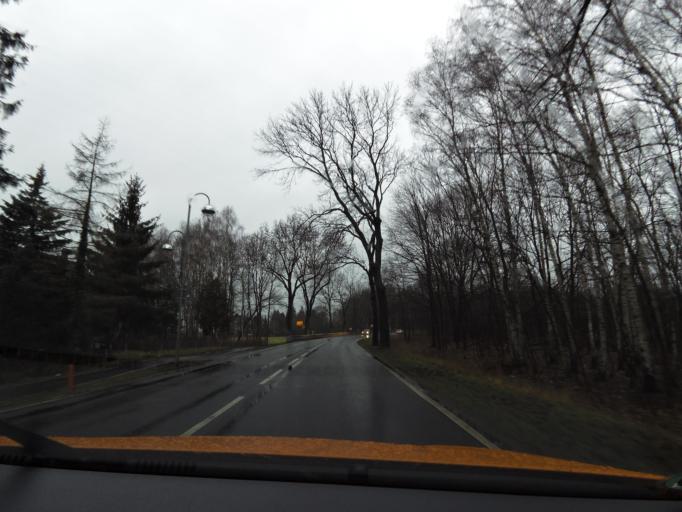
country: DE
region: Brandenburg
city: Zossen
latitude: 52.2544
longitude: 13.4480
